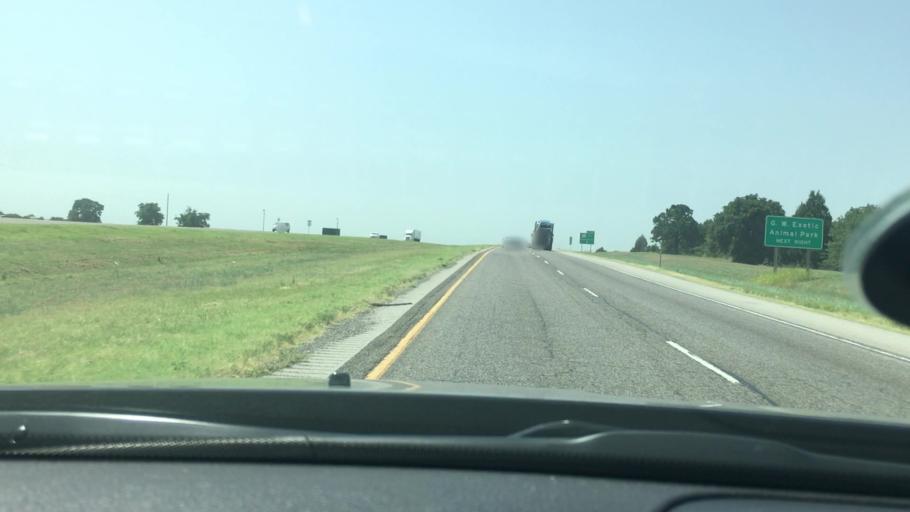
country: US
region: Oklahoma
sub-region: Garvin County
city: Wynnewood
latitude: 34.6317
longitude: -97.2174
